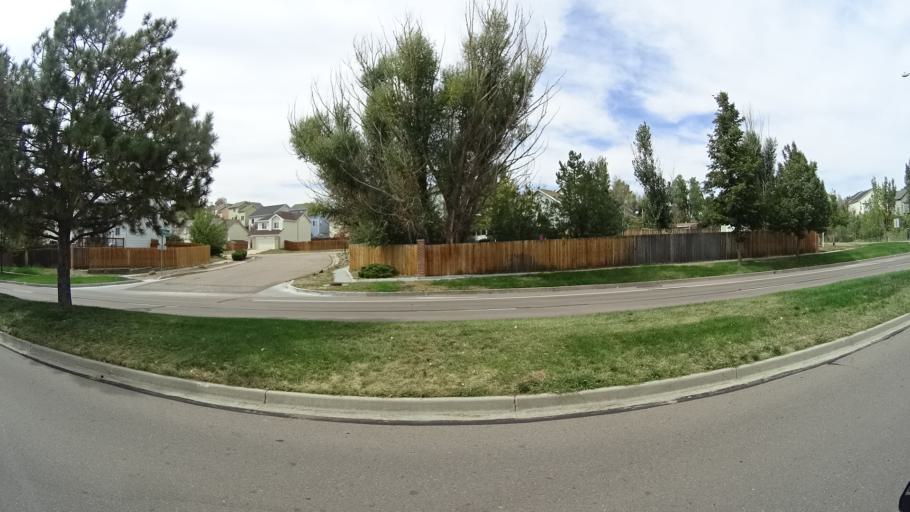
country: US
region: Colorado
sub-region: El Paso County
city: Cimarron Hills
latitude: 38.9026
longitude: -104.7088
